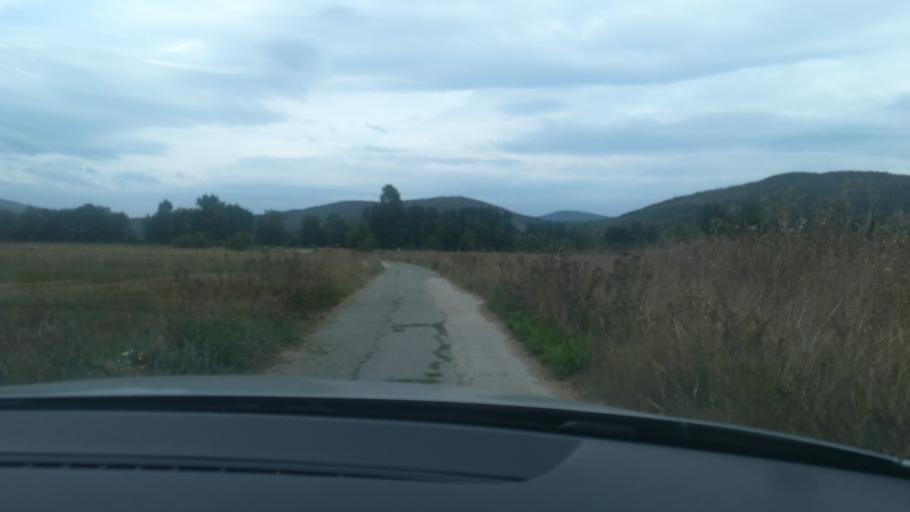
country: MK
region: Debarca
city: Belcista
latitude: 41.2958
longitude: 20.8311
